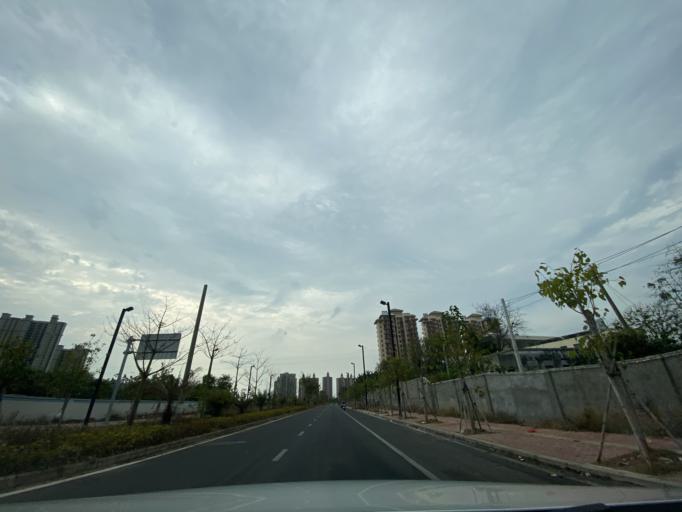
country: CN
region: Hainan
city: Yingzhou
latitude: 18.4228
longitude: 109.8878
